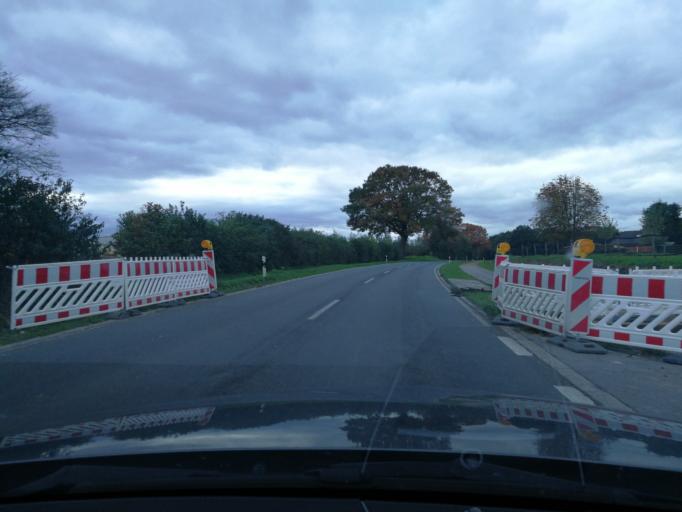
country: DE
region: North Rhine-Westphalia
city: Straelen
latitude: 51.4597
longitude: 6.2417
